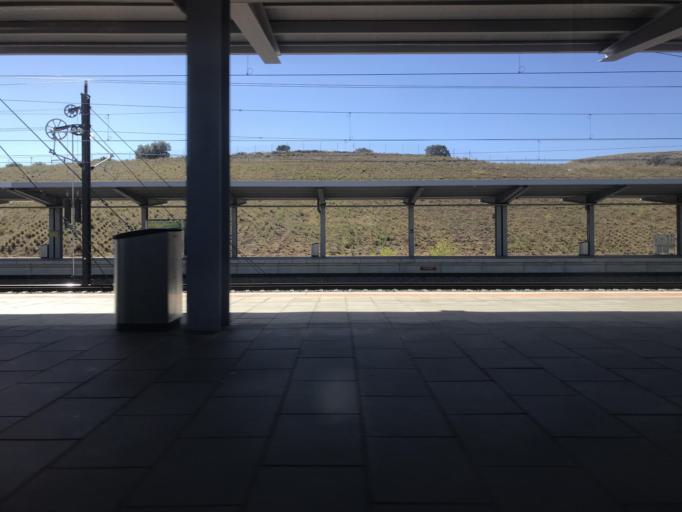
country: ES
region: Castille-La Mancha
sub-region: Provincia de Cuenca
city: Cuenca
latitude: 40.0343
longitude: -2.1436
